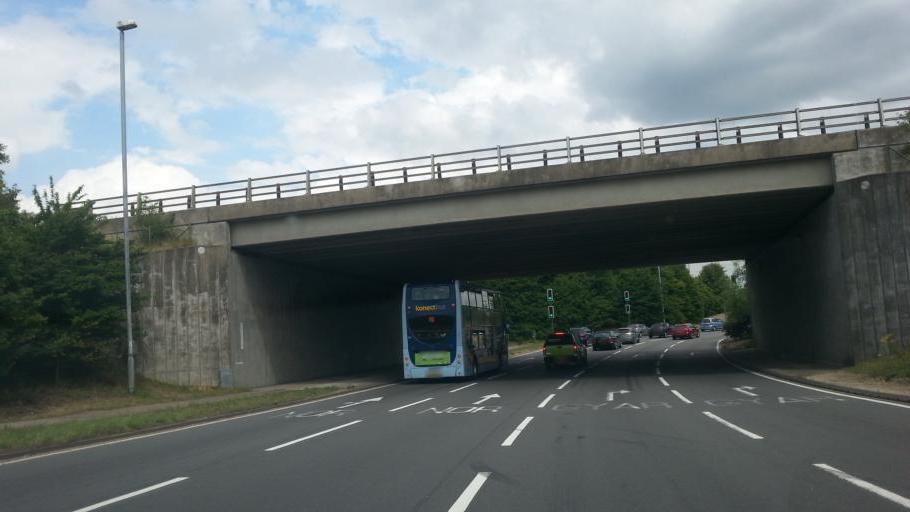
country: GB
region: England
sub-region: Norfolk
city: Cringleford
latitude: 52.6035
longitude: 1.2233
